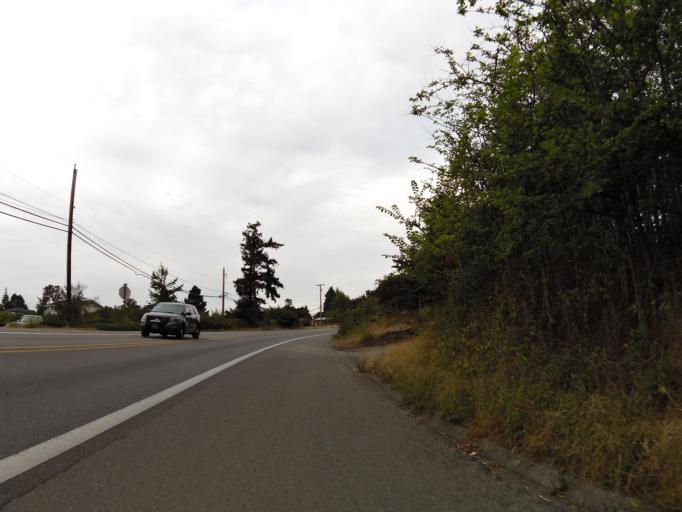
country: US
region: Washington
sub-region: Jefferson County
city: Port Townsend
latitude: 48.1033
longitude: -122.7877
